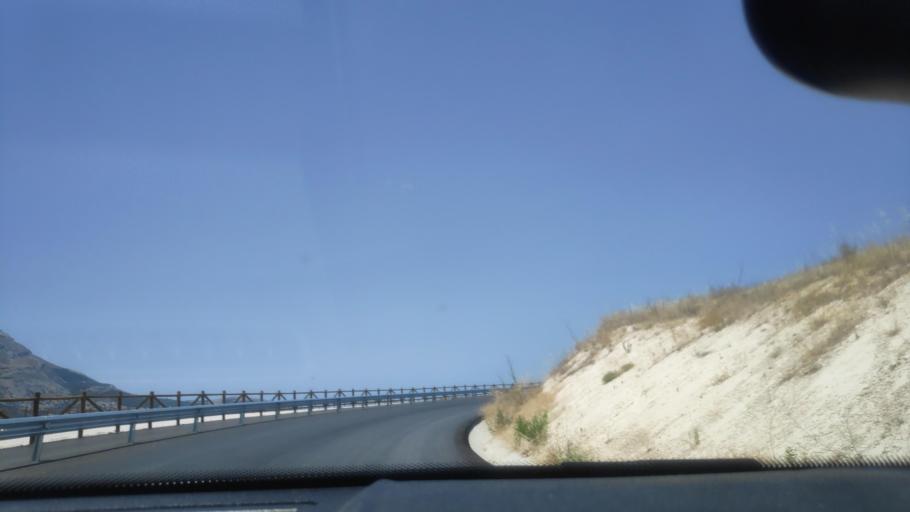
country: ES
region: Andalusia
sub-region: Provincia de Jaen
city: Jodar
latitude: 37.8085
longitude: -3.4140
